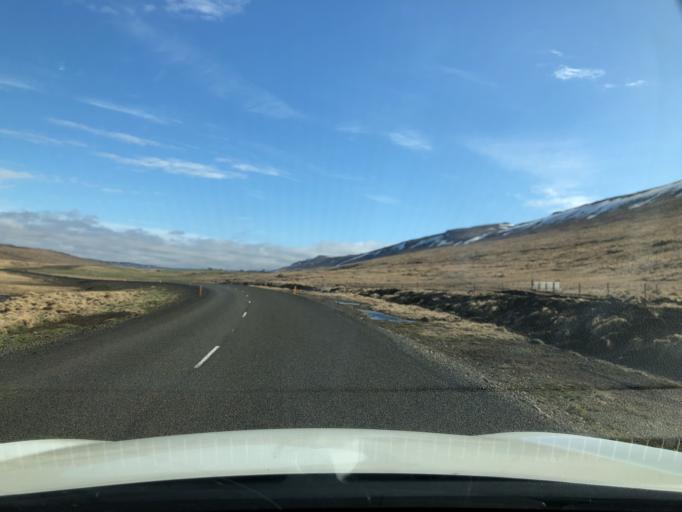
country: IS
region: West
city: Borgarnes
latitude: 65.1391
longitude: -21.5960
